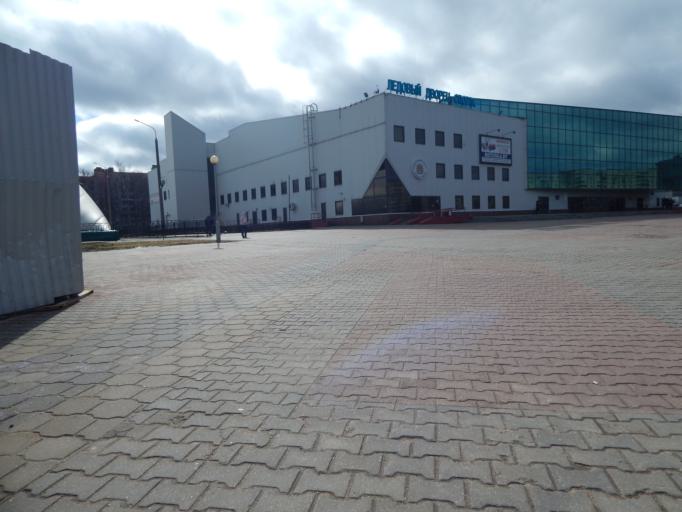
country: BY
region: Minsk
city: Novoye Medvezhino
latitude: 53.9081
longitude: 27.4875
